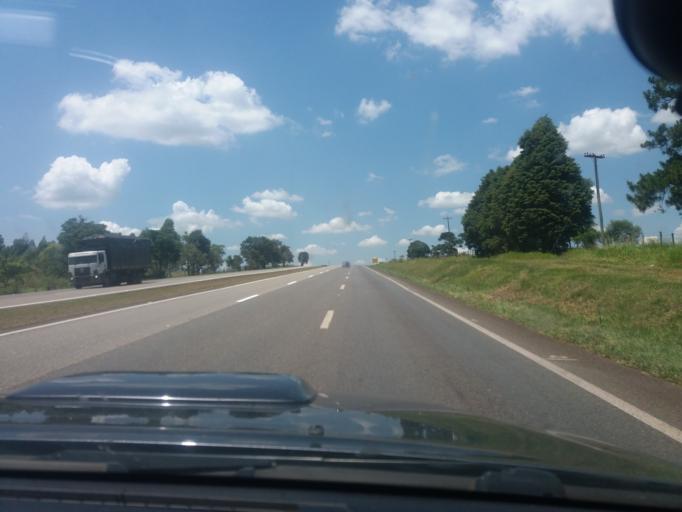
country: BR
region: Sao Paulo
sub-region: Itapetininga
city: Itapetininga
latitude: -23.4742
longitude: -47.9702
